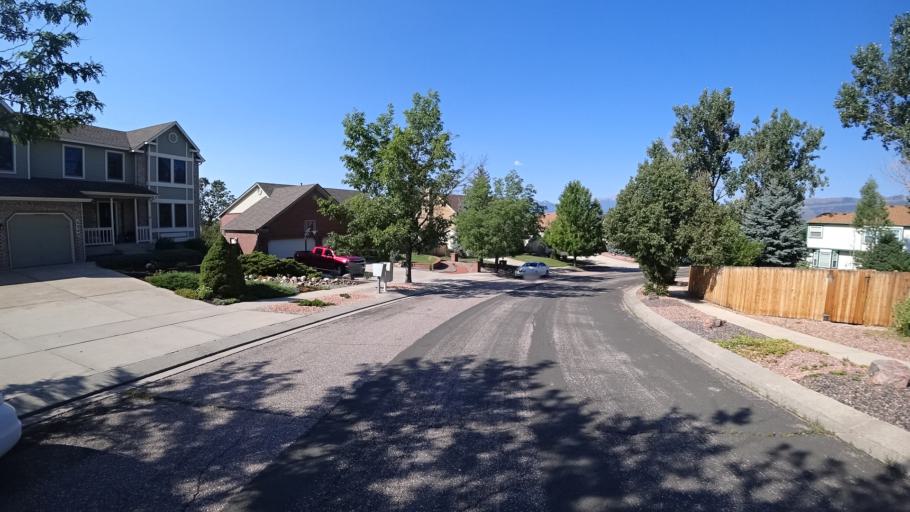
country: US
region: Colorado
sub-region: El Paso County
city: Air Force Academy
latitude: 38.9528
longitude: -104.7828
